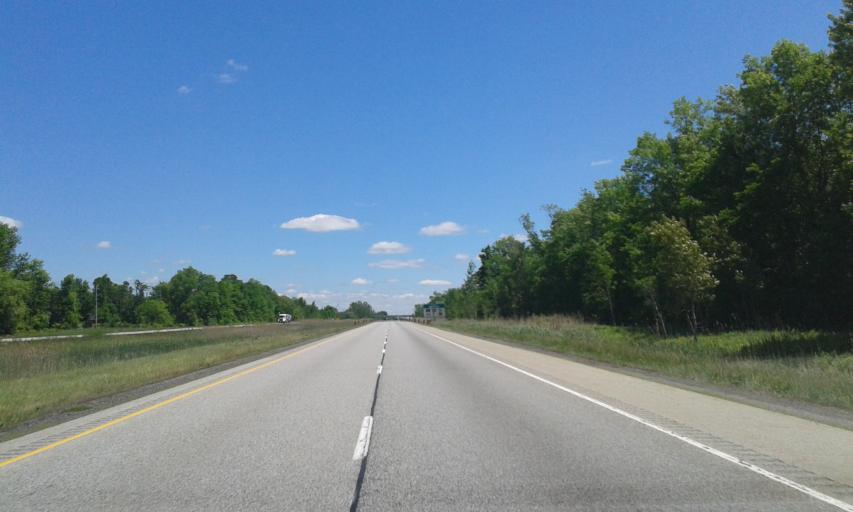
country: US
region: New York
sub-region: St. Lawrence County
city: Norfolk
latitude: 44.9331
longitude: -75.1595
